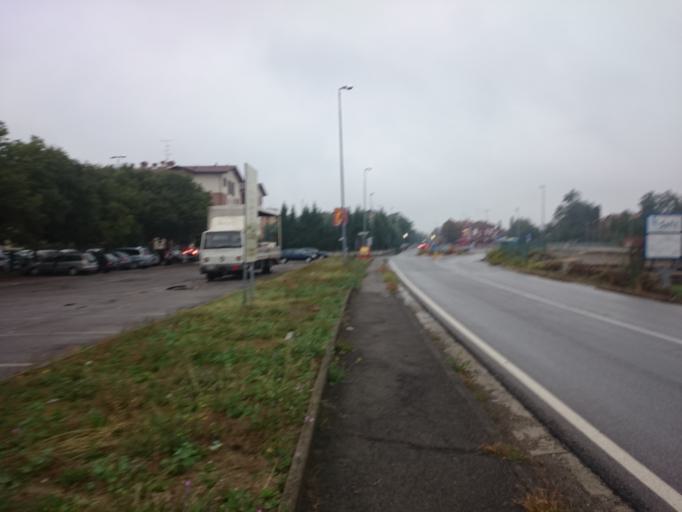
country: IT
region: Emilia-Romagna
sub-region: Provincia di Reggio Emilia
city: Scandiano
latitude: 44.5991
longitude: 10.6959
